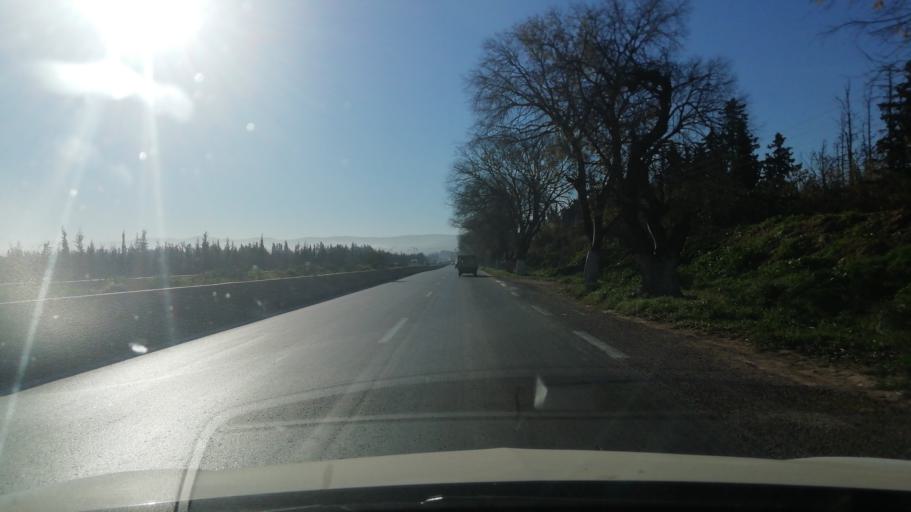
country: DZ
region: Tlemcen
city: Hennaya
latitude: 34.9717
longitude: -1.3792
